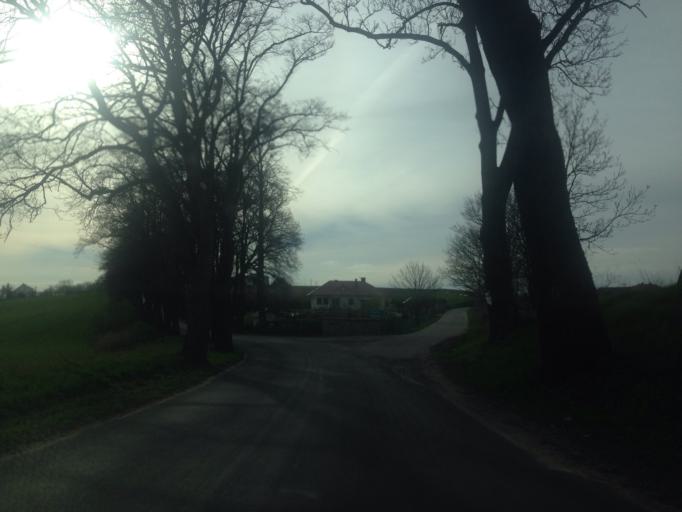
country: PL
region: Kujawsko-Pomorskie
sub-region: Powiat brodnicki
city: Jablonowo Pomorskie
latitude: 53.4283
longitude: 19.1992
